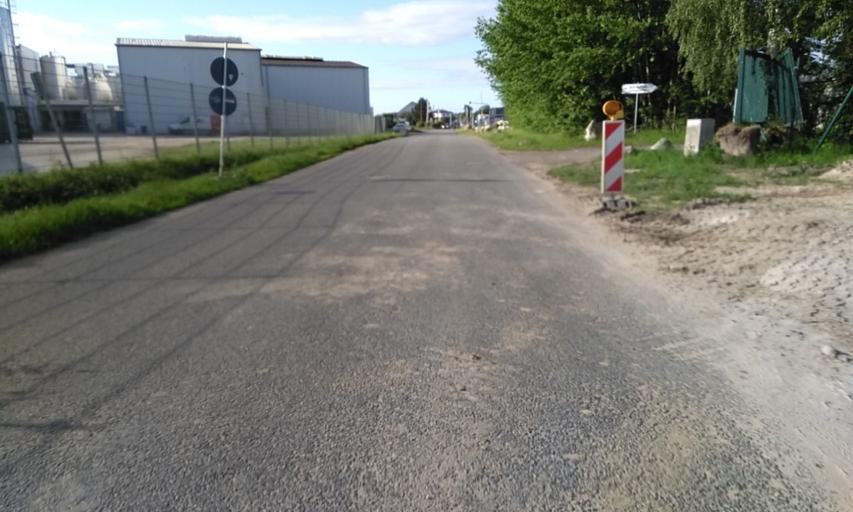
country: DE
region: Lower Saxony
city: Apensen
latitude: 53.4447
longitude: 9.6186
